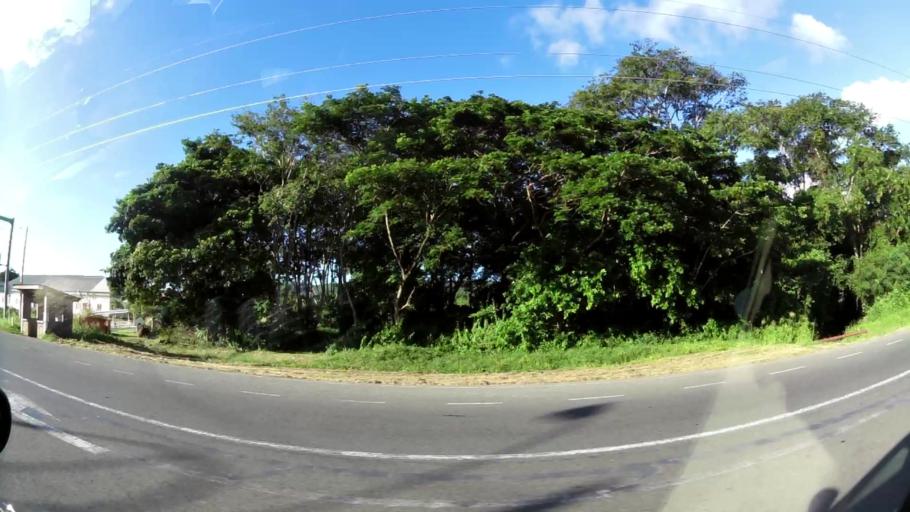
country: TT
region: Tobago
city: Scarborough
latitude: 11.1800
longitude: -60.7128
